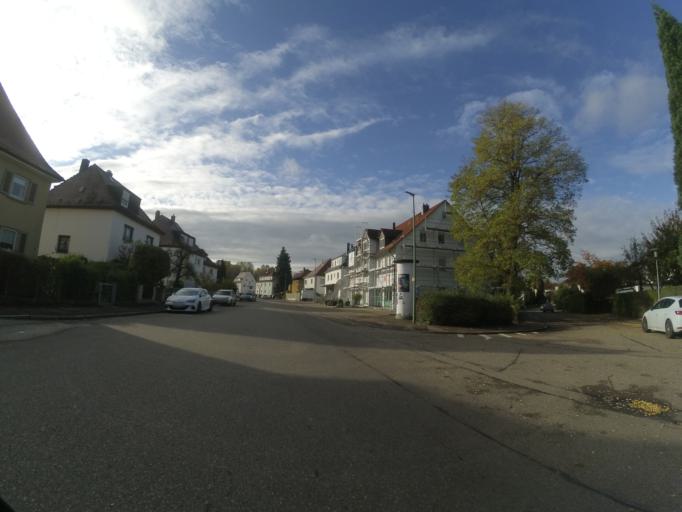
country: DE
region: Bavaria
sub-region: Swabia
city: Neu-Ulm
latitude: 48.4021
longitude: 10.0170
